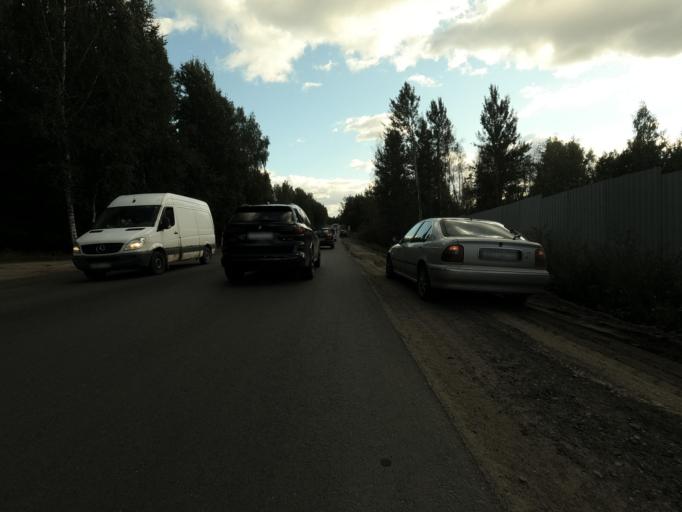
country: RU
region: Leningrad
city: Vsevolozhsk
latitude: 59.9757
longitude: 30.6535
